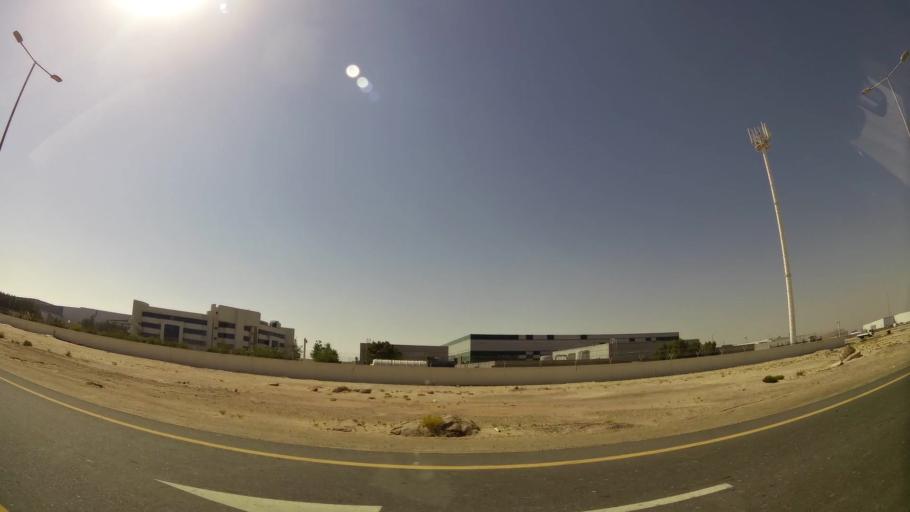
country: AE
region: Dubai
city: Dubai
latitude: 24.9176
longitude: 55.0660
